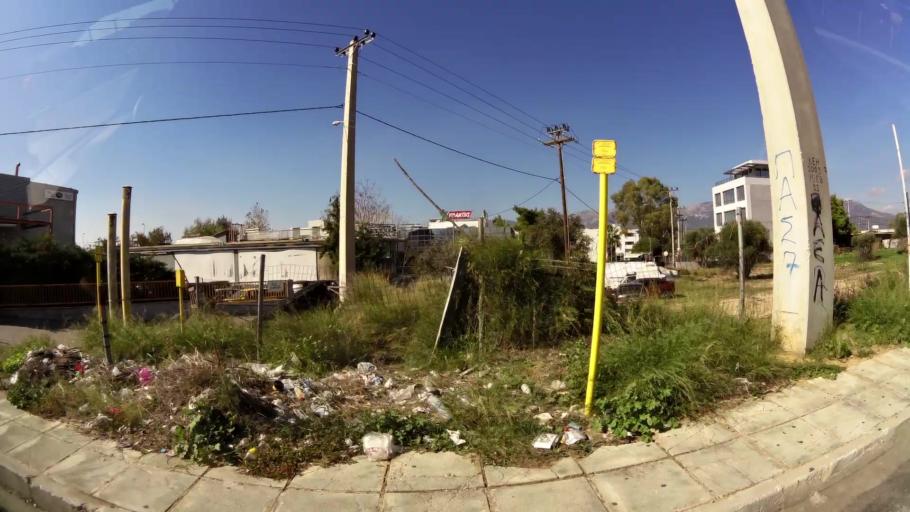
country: GR
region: Attica
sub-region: Nomarchia Athinas
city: Lykovrysi
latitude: 38.0880
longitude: 23.7879
